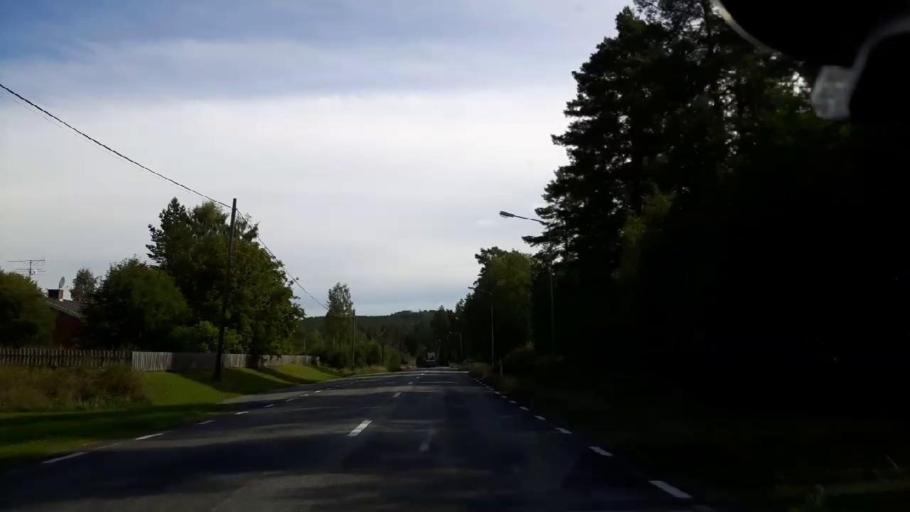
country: SE
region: Jaemtland
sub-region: Braecke Kommun
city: Braecke
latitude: 63.1627
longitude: 15.5702
